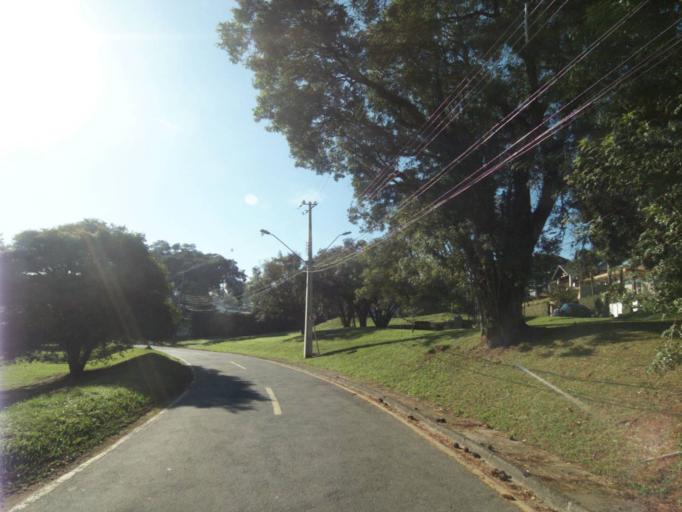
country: BR
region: Parana
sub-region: Curitiba
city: Curitiba
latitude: -25.4313
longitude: -49.3088
